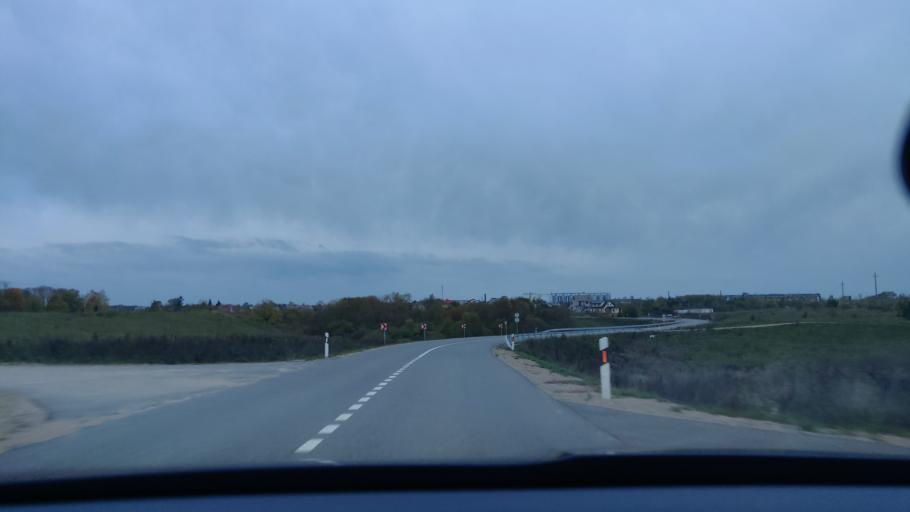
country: LT
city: Trakai
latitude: 54.6075
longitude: 24.9947
